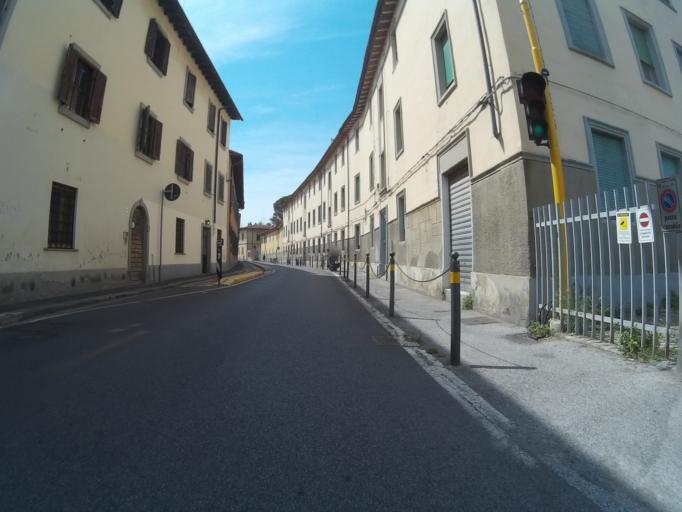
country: IT
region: Tuscany
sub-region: Provincia di Livorno
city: Livorno
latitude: 43.5367
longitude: 10.3136
